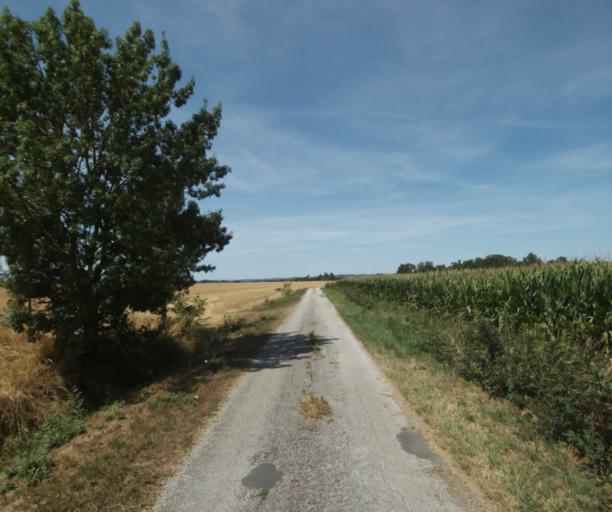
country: FR
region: Midi-Pyrenees
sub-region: Departement de la Haute-Garonne
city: Revel
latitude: 43.4941
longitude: 2.0299
